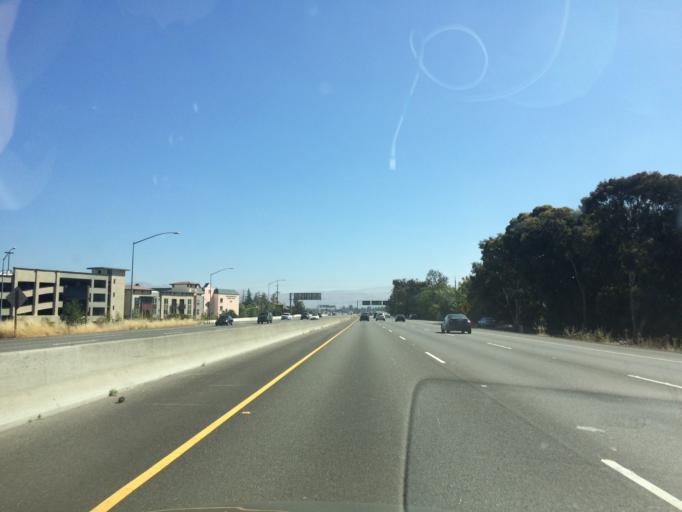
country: US
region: California
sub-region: Santa Clara County
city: San Jose
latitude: 37.3588
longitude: -121.9067
